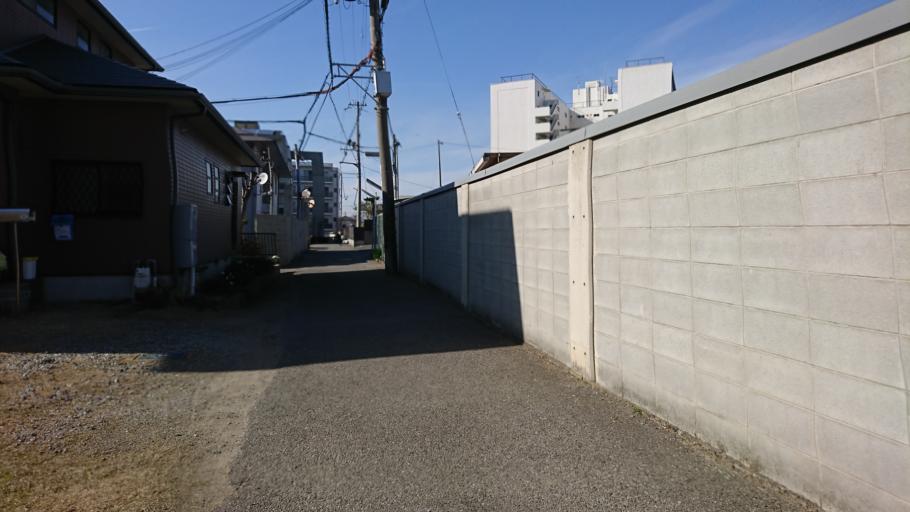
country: JP
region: Hyogo
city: Kakogawacho-honmachi
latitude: 34.7352
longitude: 134.8699
